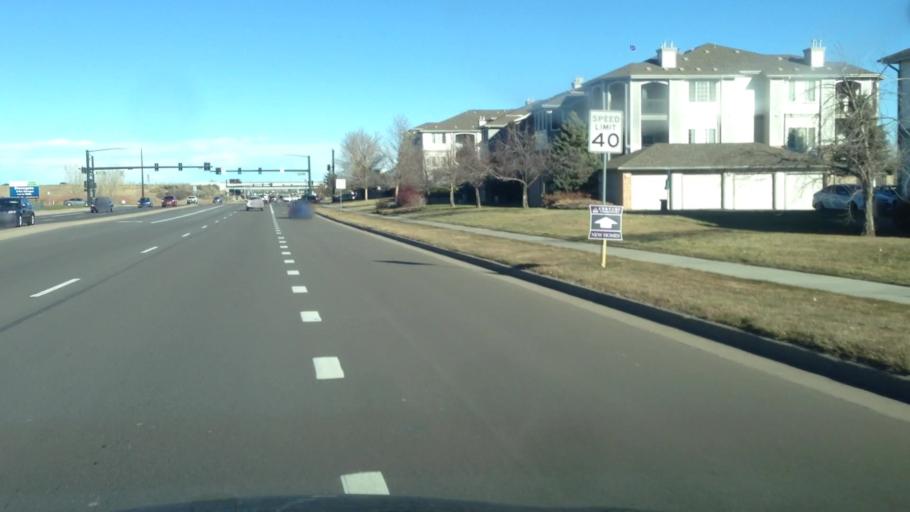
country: US
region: Colorado
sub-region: Douglas County
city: Stonegate
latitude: 39.5442
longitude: -104.7934
